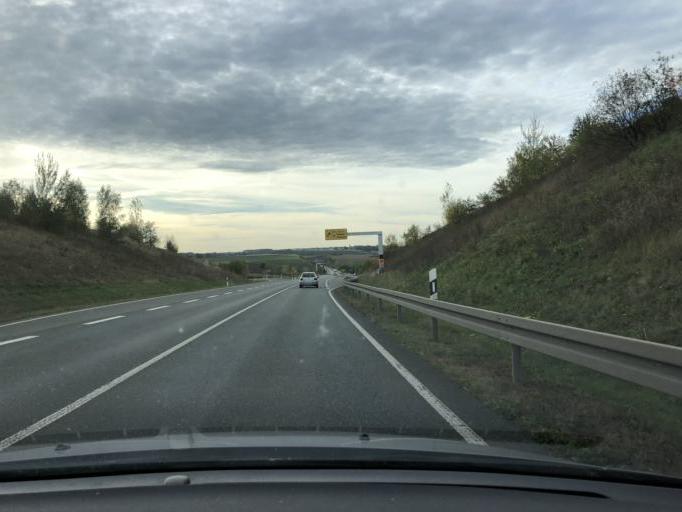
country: DE
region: Thuringia
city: Schwaara
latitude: 50.9230
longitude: 12.1349
